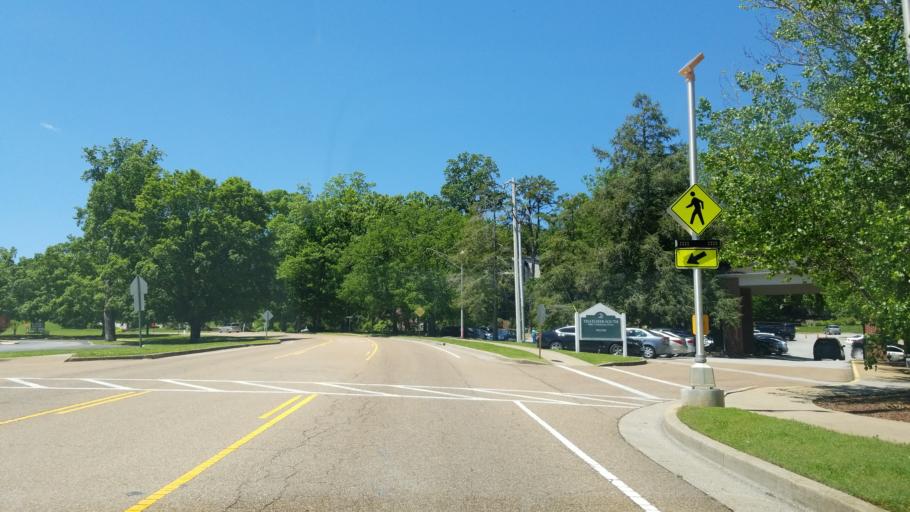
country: US
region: Tennessee
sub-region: Hamilton County
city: Collegedale
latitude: 35.0462
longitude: -85.0513
